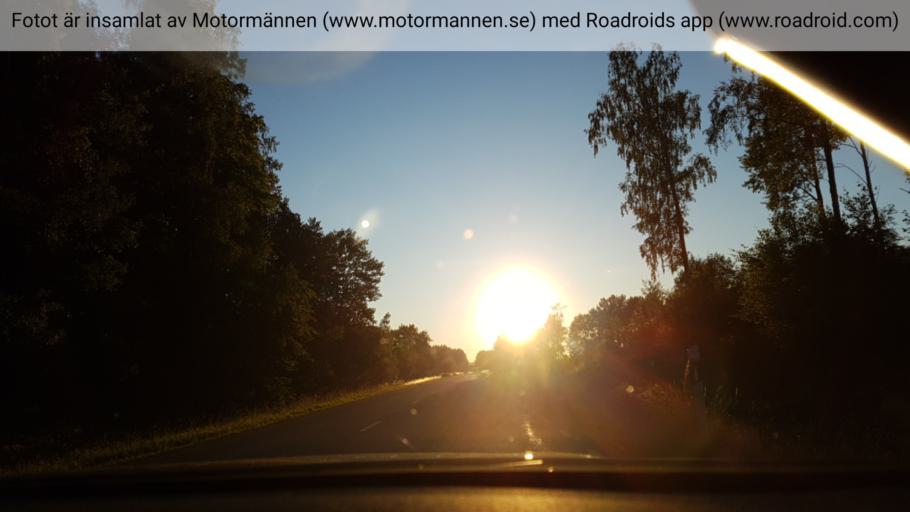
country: SE
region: Vaestra Goetaland
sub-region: Tidaholms Kommun
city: Olofstorp
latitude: 58.3651
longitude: 14.0214
